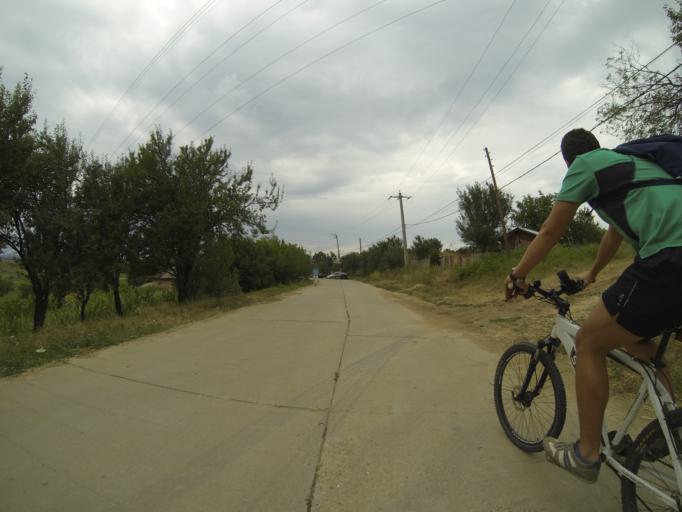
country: RO
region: Dolj
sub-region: Comuna Almaju
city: Almaju
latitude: 44.4518
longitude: 23.7033
